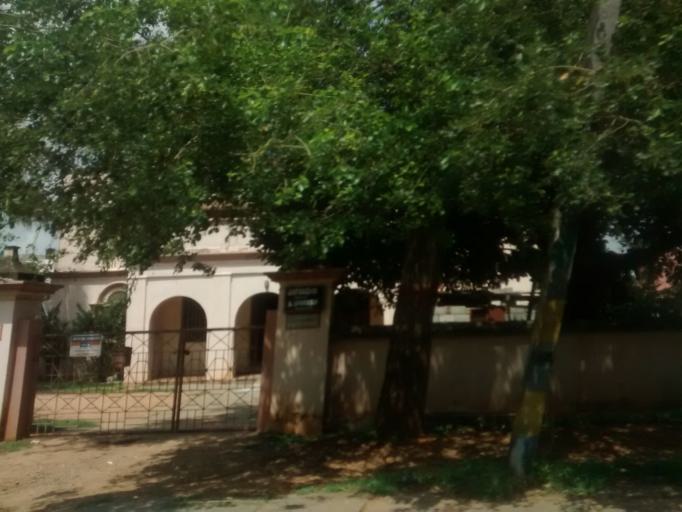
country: IN
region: Karnataka
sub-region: Mysore
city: Mysore
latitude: 12.3038
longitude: 76.6435
